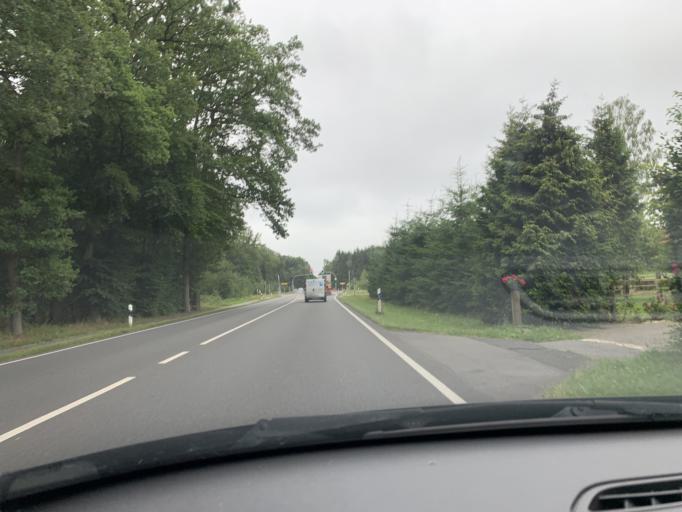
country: DE
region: Lower Saxony
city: Haselunne
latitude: 52.6605
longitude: 7.4791
